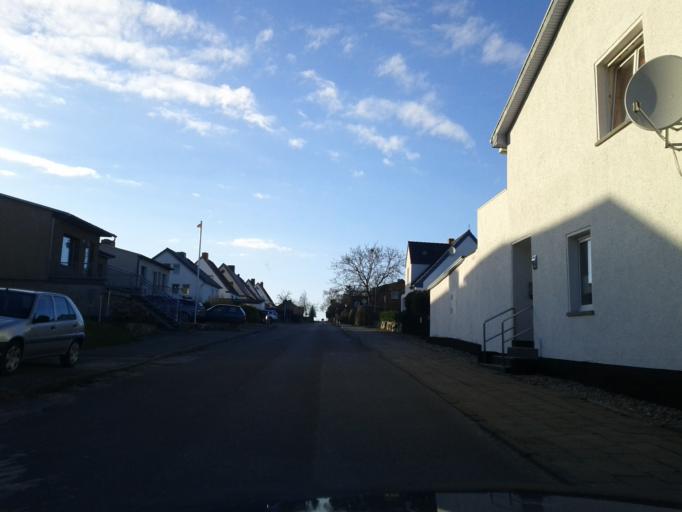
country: DE
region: Mecklenburg-Vorpommern
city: Blowatz
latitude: 53.9960
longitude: 11.4364
